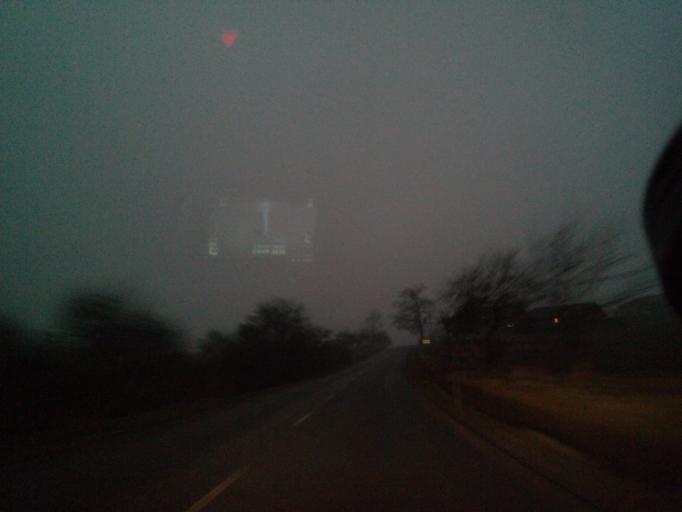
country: SK
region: Presovsky
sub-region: Okres Presov
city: Presov
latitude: 49.0184
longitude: 21.1877
